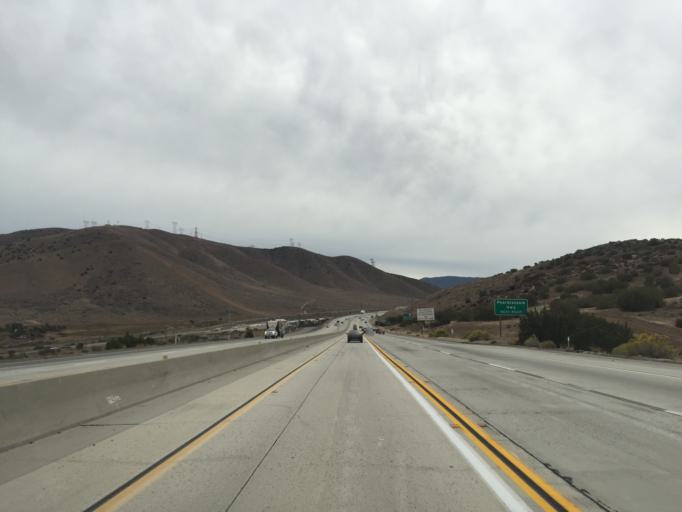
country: US
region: California
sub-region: Los Angeles County
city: Vincent
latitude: 34.5186
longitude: -118.1109
